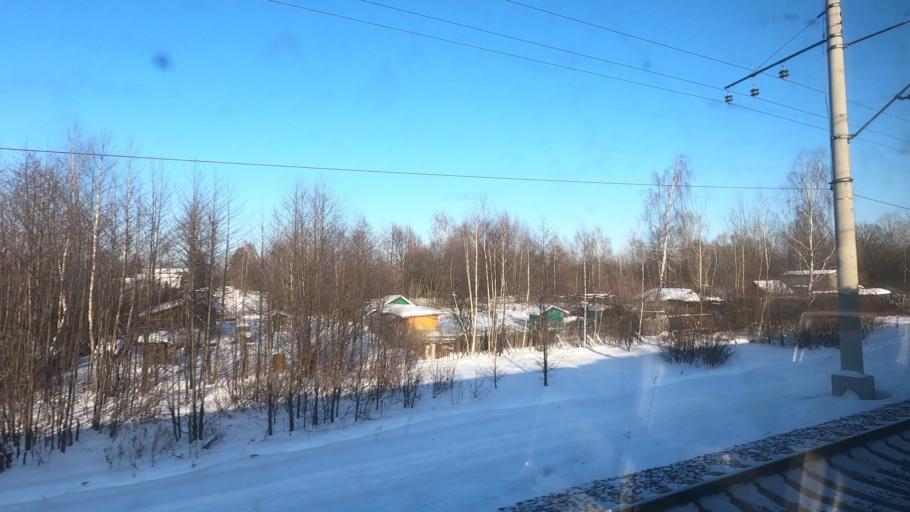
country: RU
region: Moskovskaya
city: Imeni Vorovskogo
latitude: 55.7218
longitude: 38.3108
